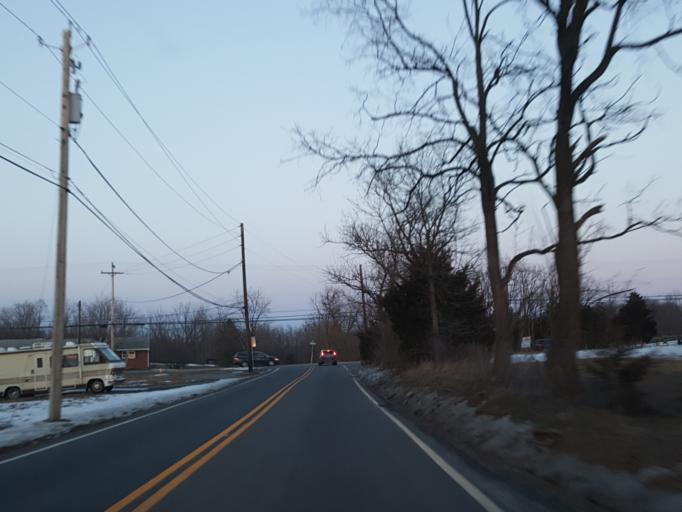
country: US
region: Pennsylvania
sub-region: Dauphin County
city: Skyline View
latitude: 40.3185
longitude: -76.7031
